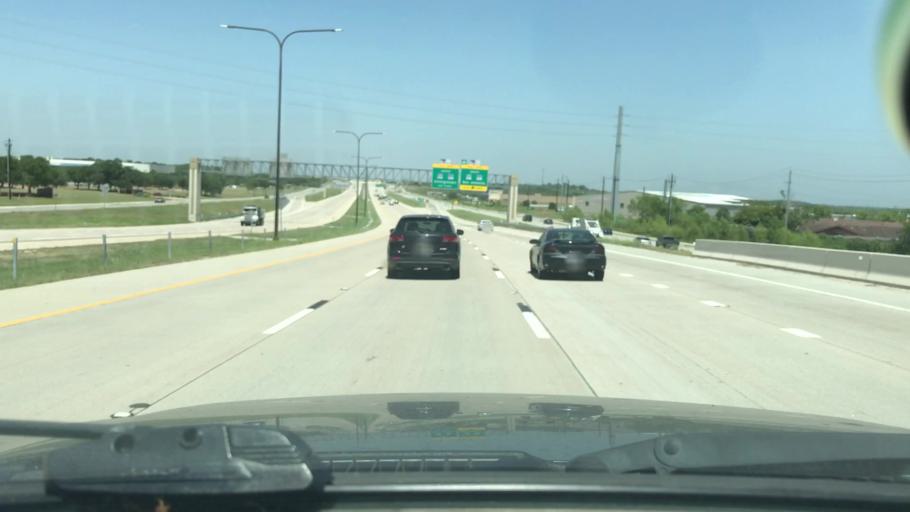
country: US
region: Texas
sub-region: Travis County
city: Manor
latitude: 30.3309
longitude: -97.6216
